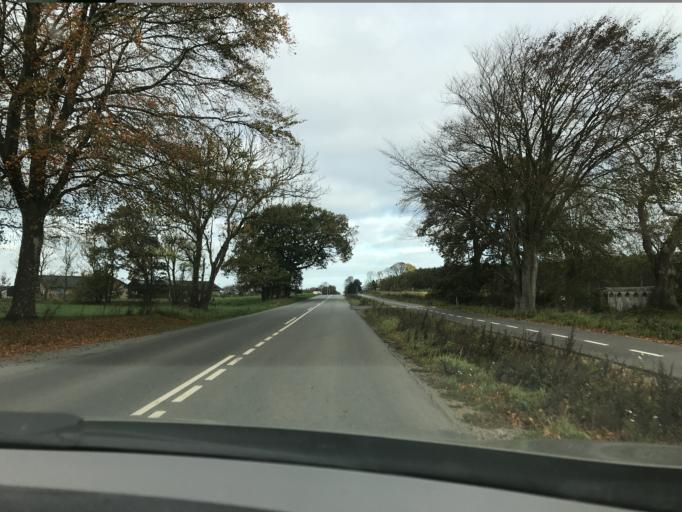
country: DK
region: South Denmark
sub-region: Kolding Kommune
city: Kolding
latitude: 55.5521
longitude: 9.4115
